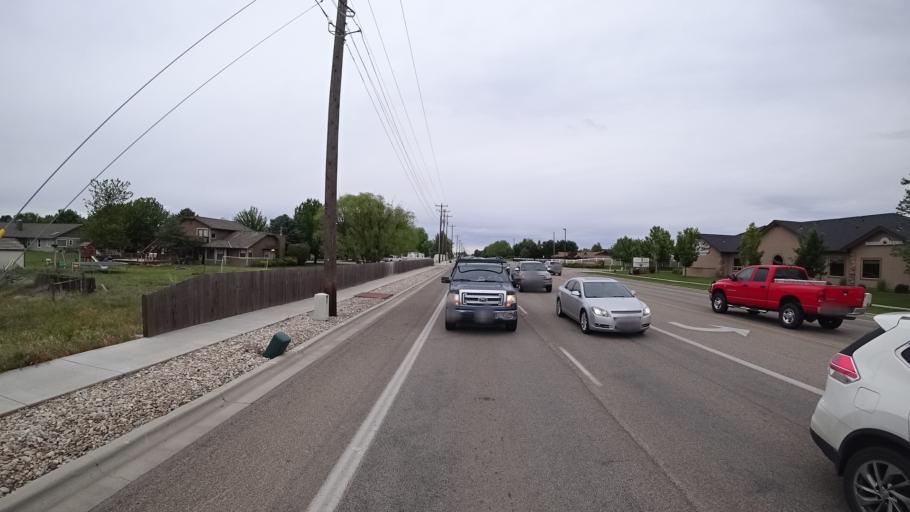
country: US
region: Idaho
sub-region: Ada County
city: Meridian
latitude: 43.6338
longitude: -116.3594
